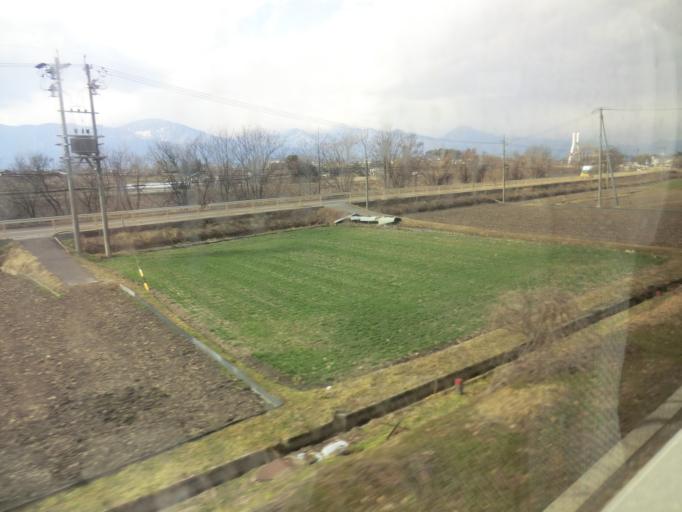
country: JP
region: Nagano
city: Matsumoto
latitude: 36.2600
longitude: 137.9489
